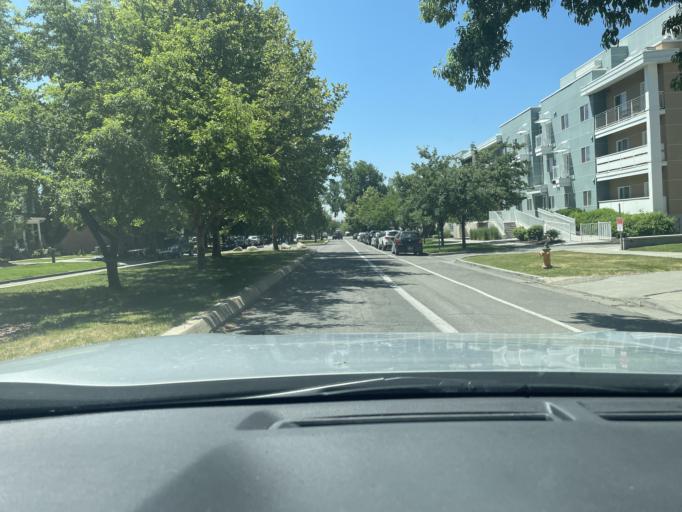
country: US
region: Utah
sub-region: Salt Lake County
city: Salt Lake City
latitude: 40.7625
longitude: -111.8740
